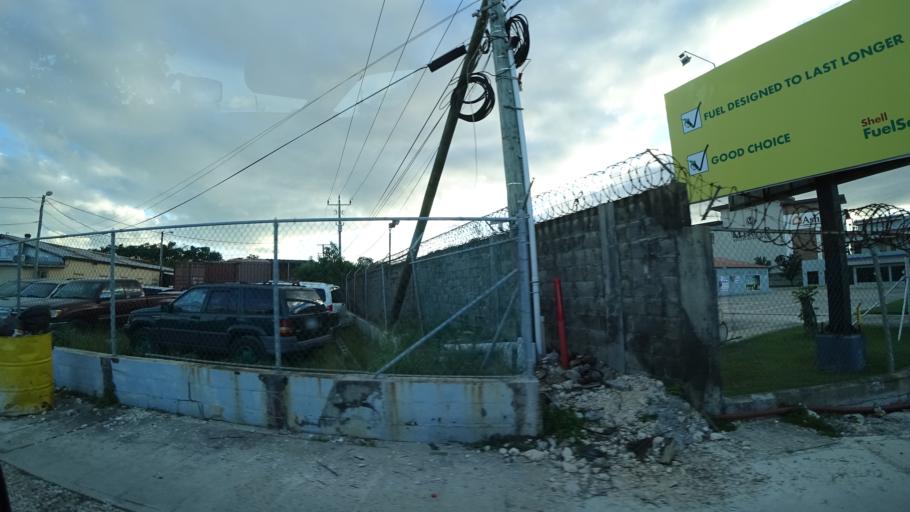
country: BZ
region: Belize
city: Belize City
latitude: 17.5106
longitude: -88.2123
